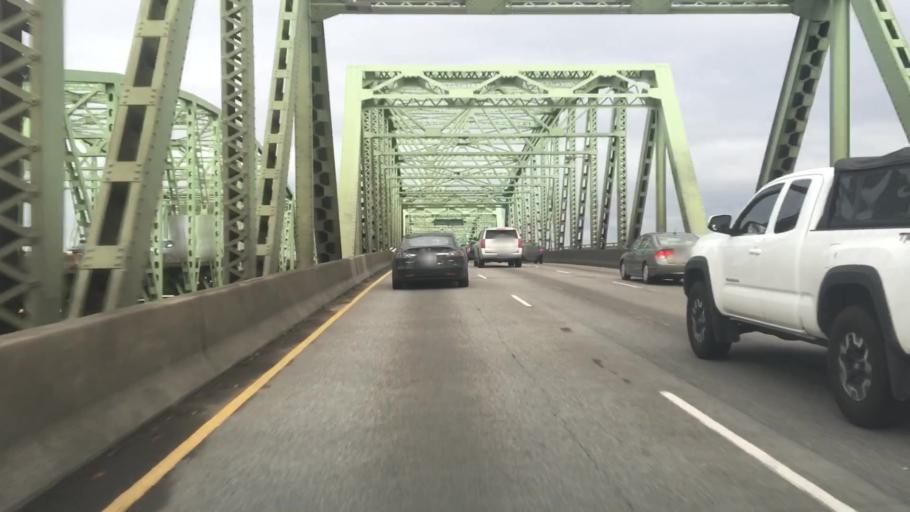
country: US
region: Washington
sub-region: Clark County
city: Vancouver
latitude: 45.6157
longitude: -122.6764
